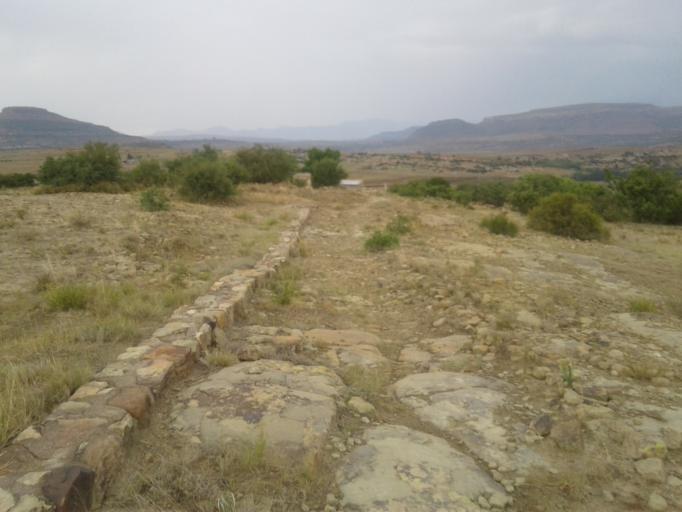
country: LS
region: Quthing
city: Quthing
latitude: -30.3825
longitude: 27.5621
